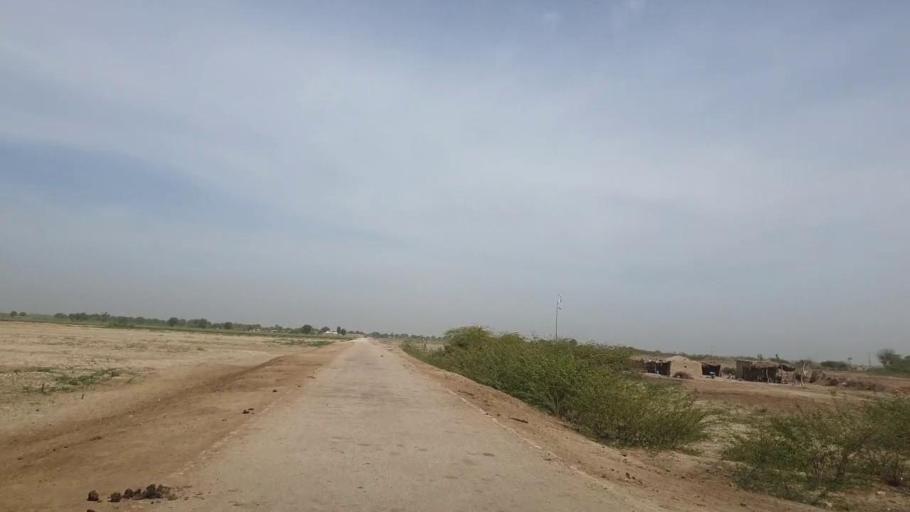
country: PK
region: Sindh
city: Kunri
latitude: 25.1711
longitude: 69.6175
